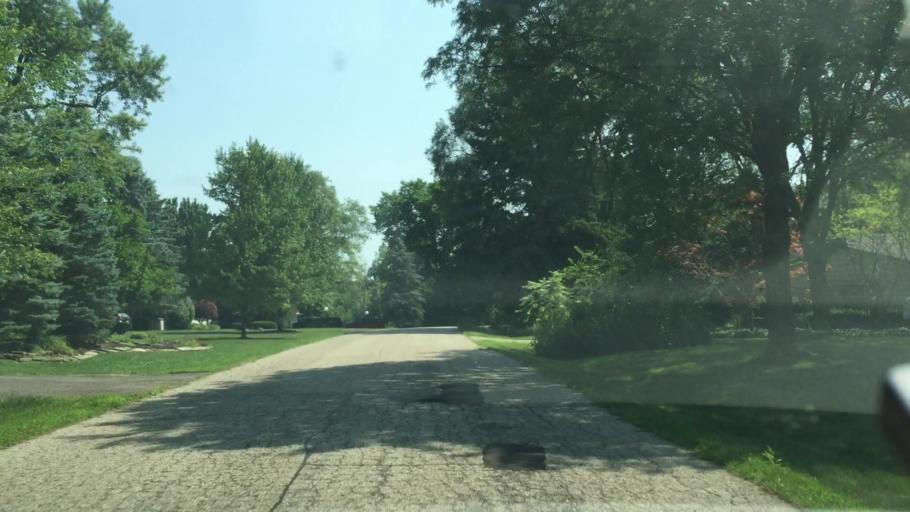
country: US
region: Michigan
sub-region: Oakland County
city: Franklin
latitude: 42.5548
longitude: -83.3184
